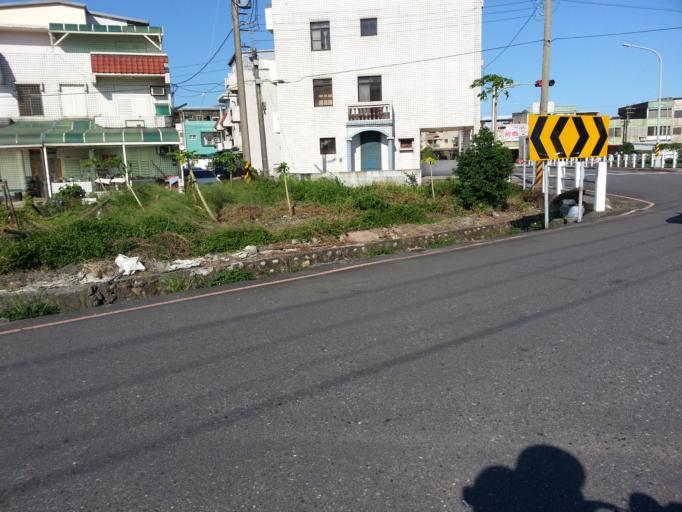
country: TW
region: Taiwan
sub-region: Yilan
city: Yilan
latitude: 24.6165
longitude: 121.8286
